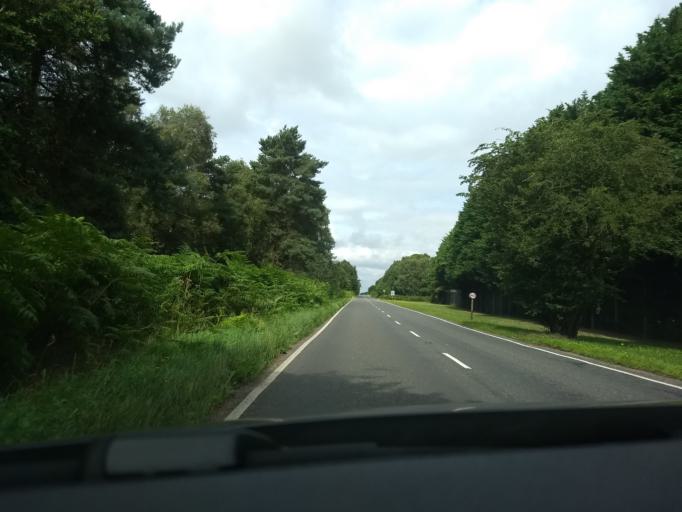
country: GB
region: England
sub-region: Suffolk
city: Woodbridge
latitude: 52.0829
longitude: 1.3780
